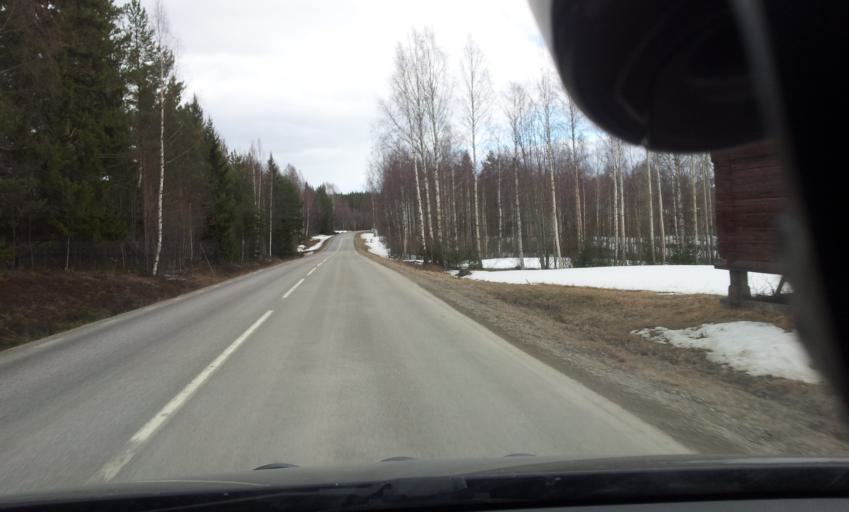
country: SE
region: Gaevleborg
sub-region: Ljusdals Kommun
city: Farila
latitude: 62.1262
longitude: 15.7131
